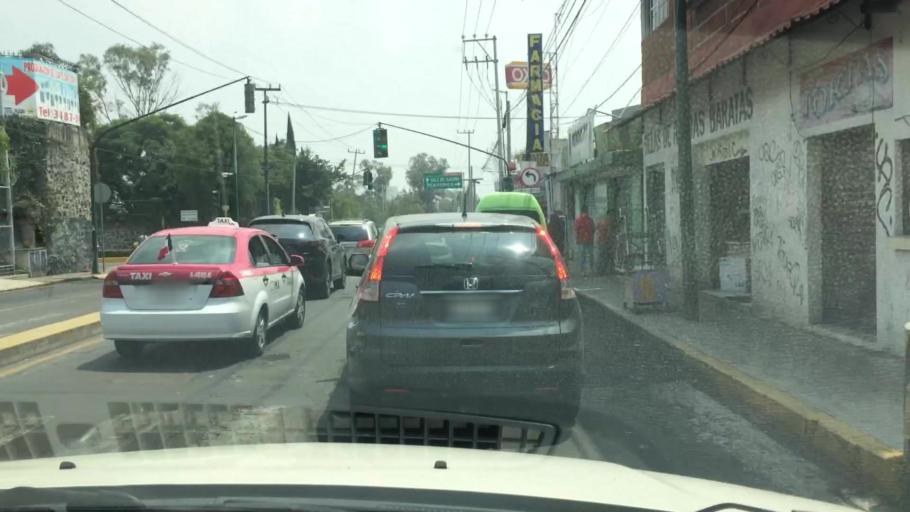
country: MX
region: Mexico City
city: Tlalpan
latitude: 19.3041
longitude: -99.1599
